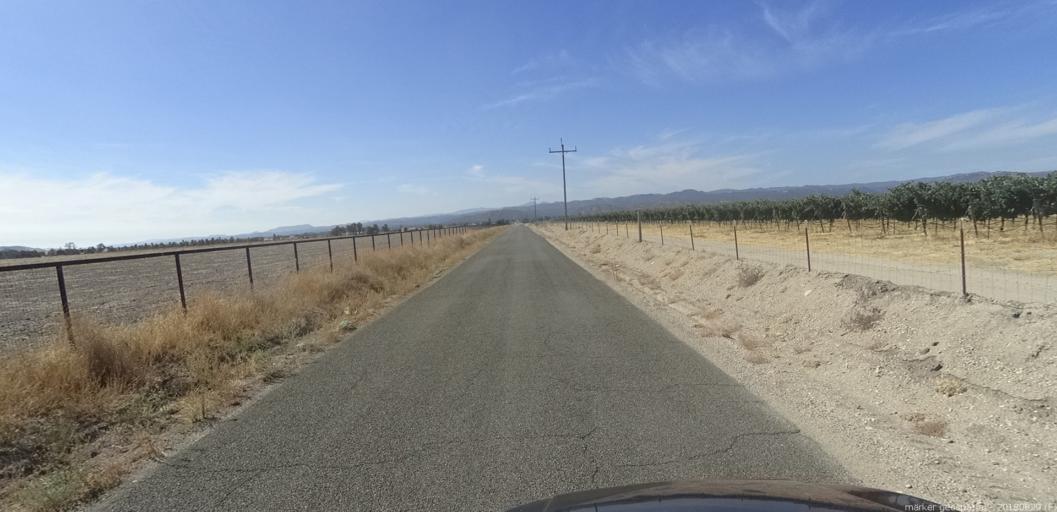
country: US
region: California
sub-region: Monterey County
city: King City
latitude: 35.9616
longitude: -121.0818
